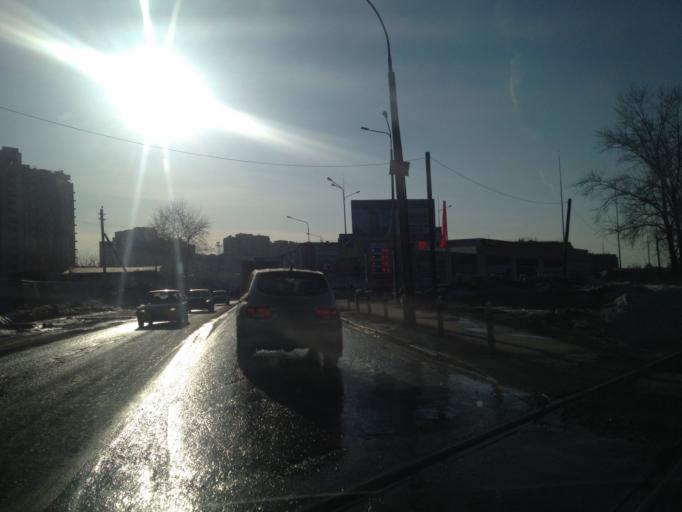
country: RU
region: Sverdlovsk
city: Yekaterinburg
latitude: 56.8563
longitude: 60.5785
